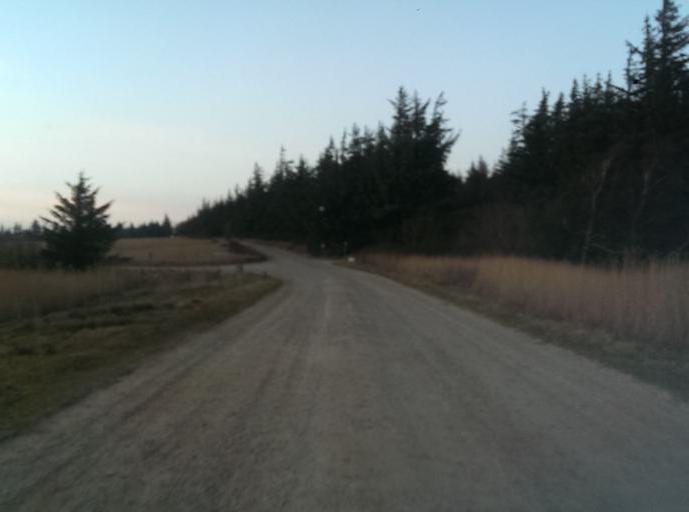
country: DK
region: South Denmark
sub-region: Varde Kommune
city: Oksbol
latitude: 55.5576
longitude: 8.3177
